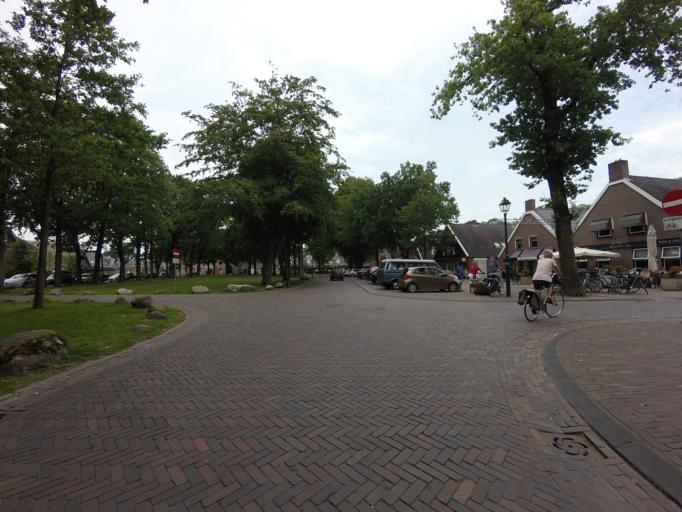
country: NL
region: Drenthe
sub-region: Gemeente Westerveld
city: Dwingeloo
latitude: 52.8332
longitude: 6.3663
